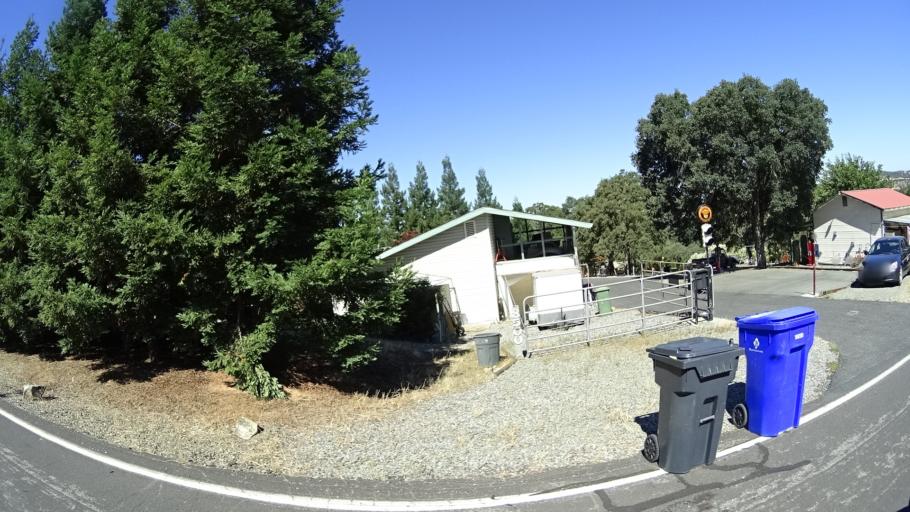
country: US
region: California
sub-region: Calaveras County
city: Rancho Calaveras
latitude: 38.1080
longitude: -120.8724
